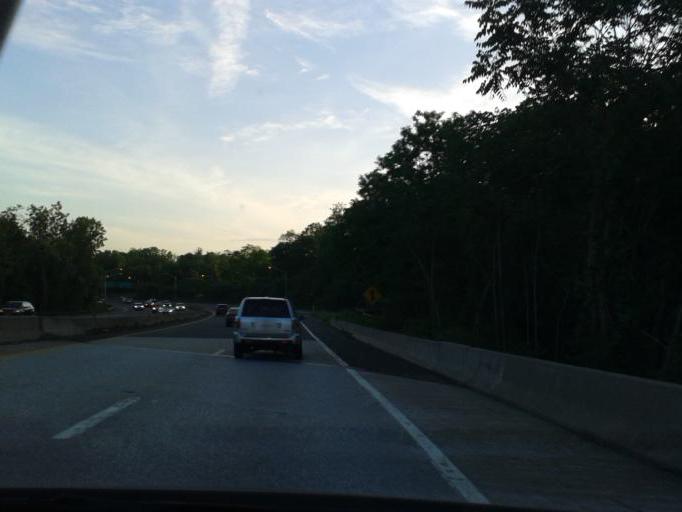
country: US
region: New York
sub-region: Westchester County
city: Tuckahoe
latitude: 40.9439
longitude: -73.8017
